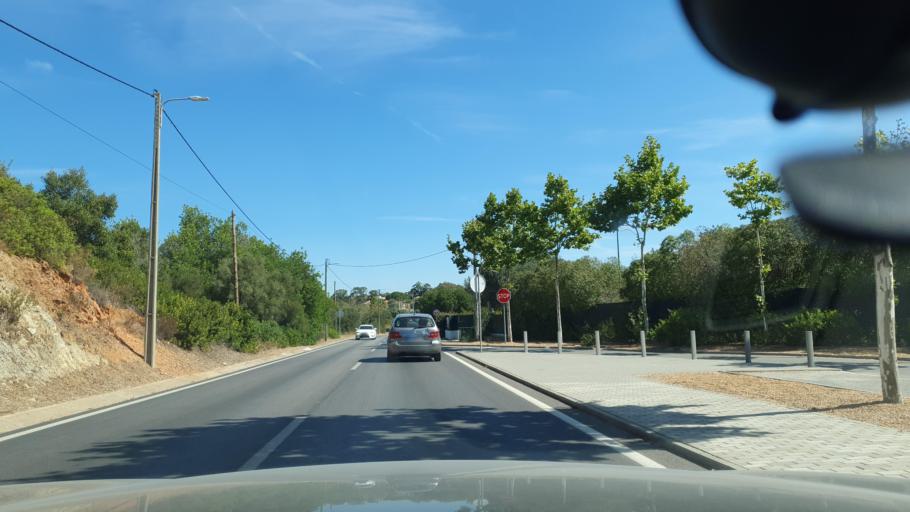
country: PT
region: Faro
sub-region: Albufeira
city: Guia
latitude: 37.1075
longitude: -8.3075
